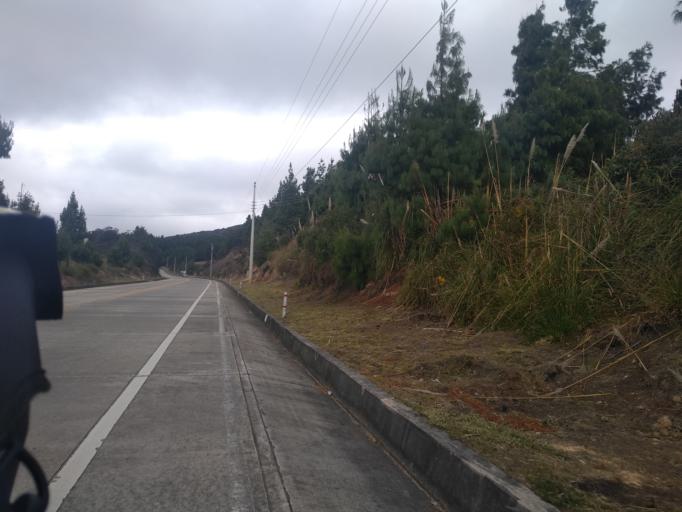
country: EC
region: Azuay
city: Cuenca
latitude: -3.3620
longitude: -79.1934
